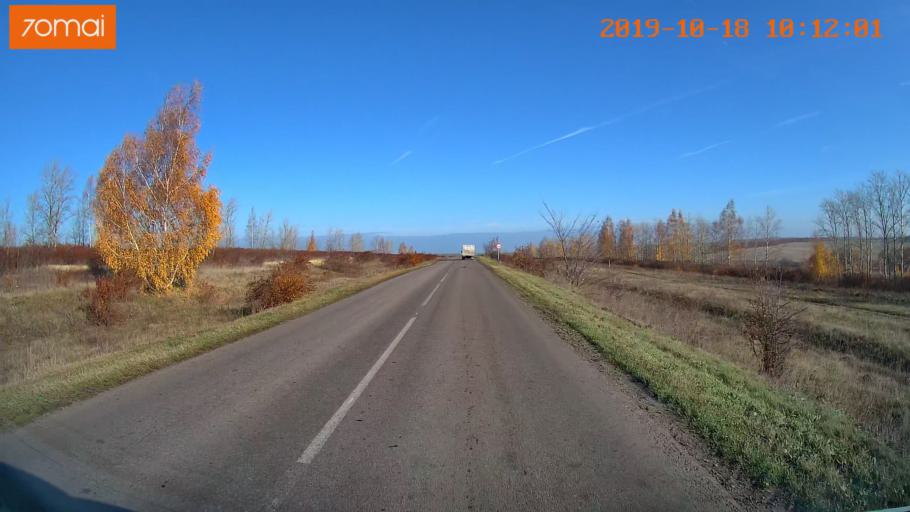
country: RU
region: Tula
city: Kurkino
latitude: 53.3890
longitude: 38.5044
